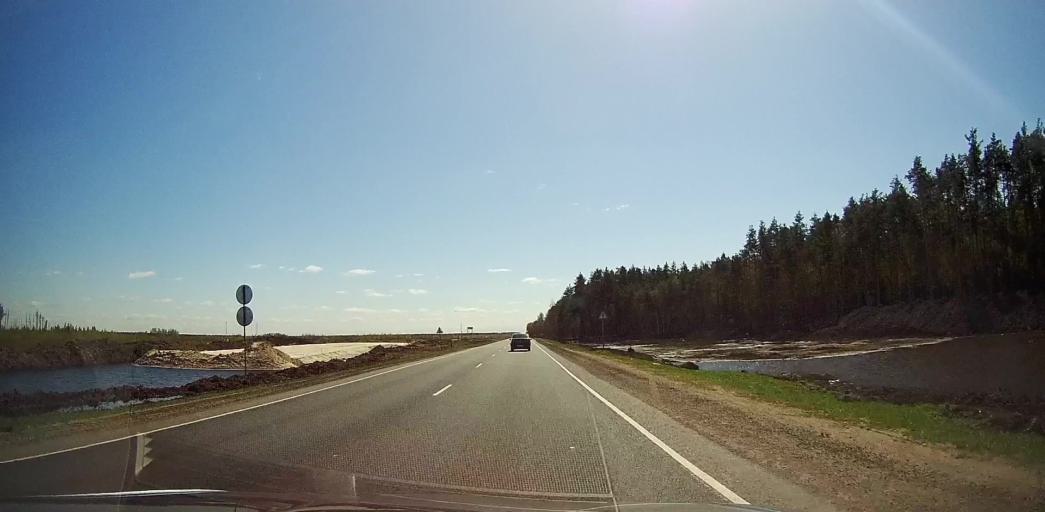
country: RU
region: Moskovskaya
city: Gzhel'
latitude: 55.5939
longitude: 38.3808
